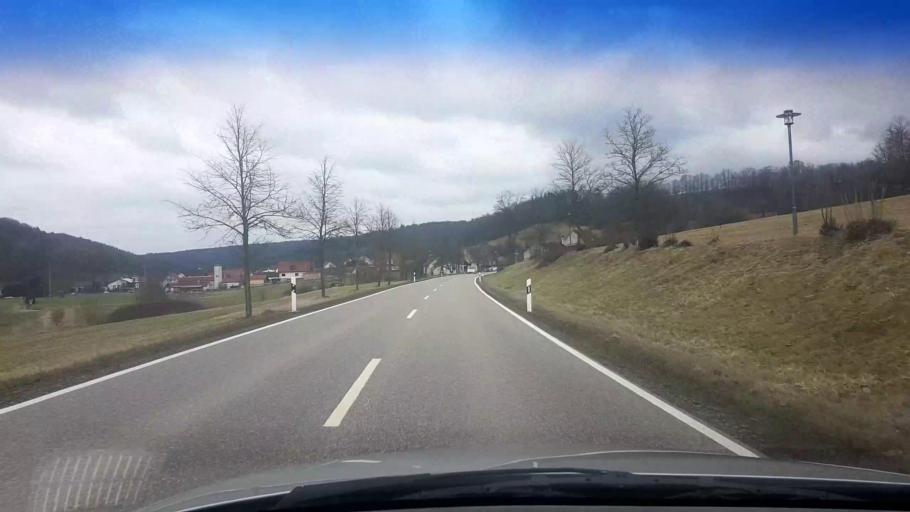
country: DE
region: Bavaria
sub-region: Regierungsbezirk Unterfranken
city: Sand
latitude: 49.9461
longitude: 10.6021
